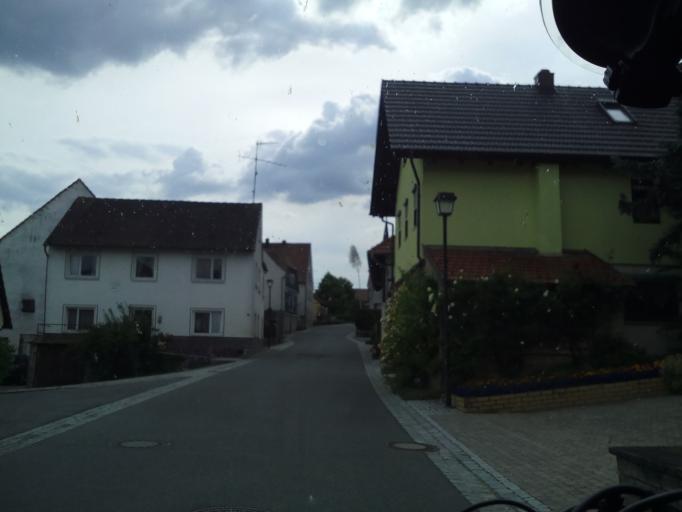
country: DE
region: Bavaria
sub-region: Regierungsbezirk Unterfranken
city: Pfarrweisach
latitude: 50.2077
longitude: 10.7450
